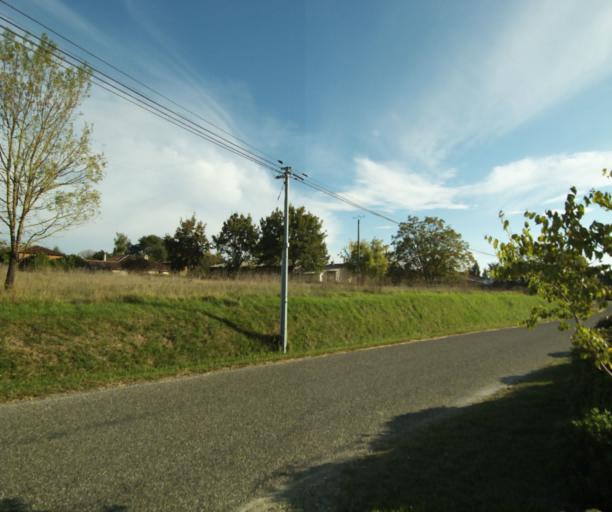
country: FR
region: Midi-Pyrenees
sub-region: Departement du Gers
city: Eauze
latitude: 43.8640
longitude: 0.0272
